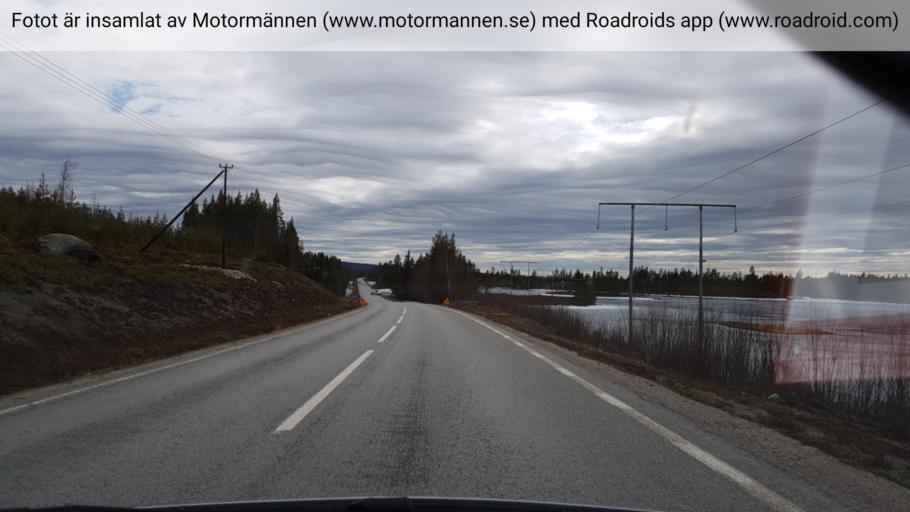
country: SE
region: Vaesterbotten
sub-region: Asele Kommun
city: Asele
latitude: 63.9104
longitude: 17.2236
